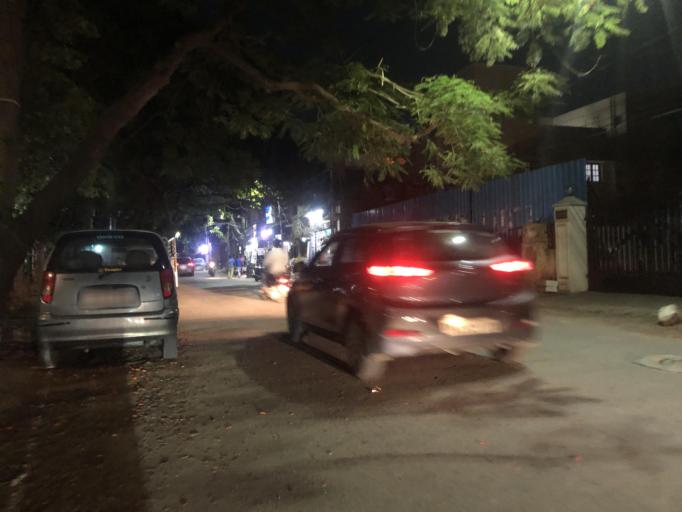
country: IN
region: Tamil Nadu
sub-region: Chennai
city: Gandhi Nagar
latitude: 13.0335
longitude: 80.2547
